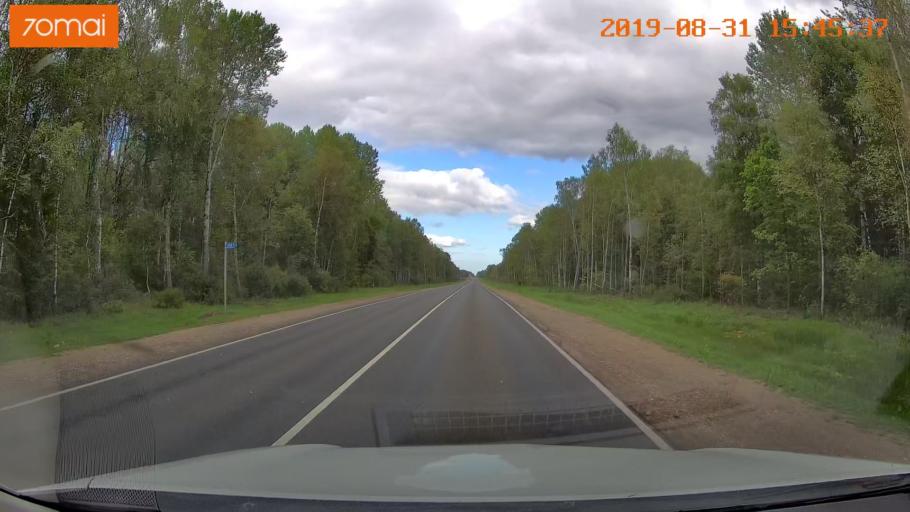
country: RU
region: Kaluga
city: Mosal'sk
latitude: 54.6675
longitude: 34.9637
